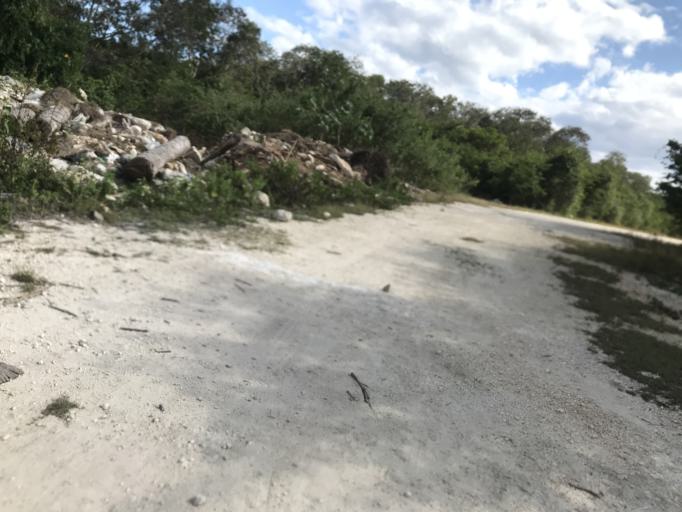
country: CU
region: Cienfuegos
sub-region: Municipio de Aguada de Pasajeros
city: Aguada de Pasajeros
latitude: 22.0756
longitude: -81.0368
